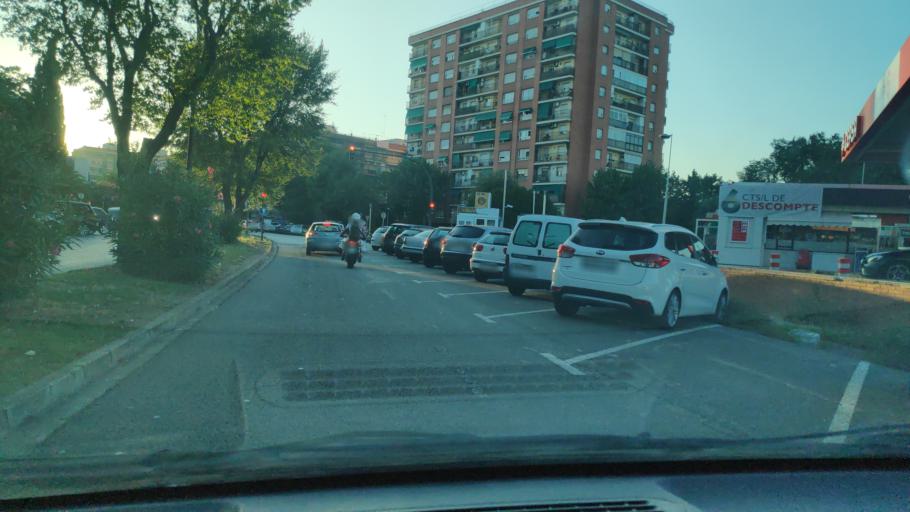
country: ES
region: Catalonia
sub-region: Provincia de Barcelona
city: Ripollet
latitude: 41.4890
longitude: 2.1516
